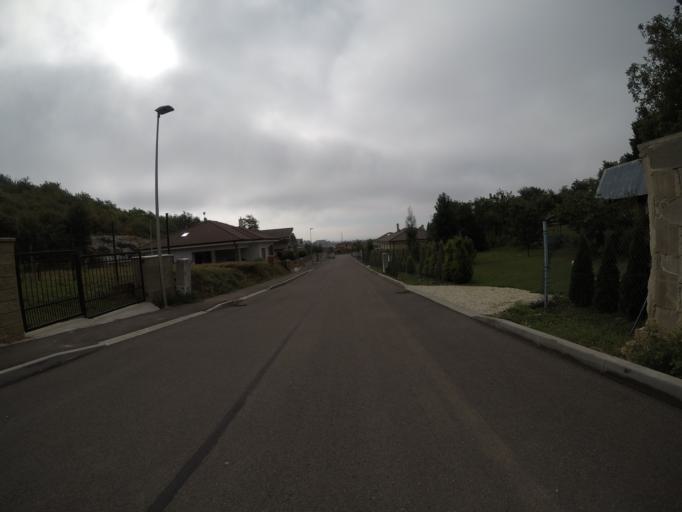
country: SK
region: Trenciansky
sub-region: Okres Nove Mesto nad Vahom
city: Nove Mesto nad Vahom
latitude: 48.7598
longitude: 17.8114
